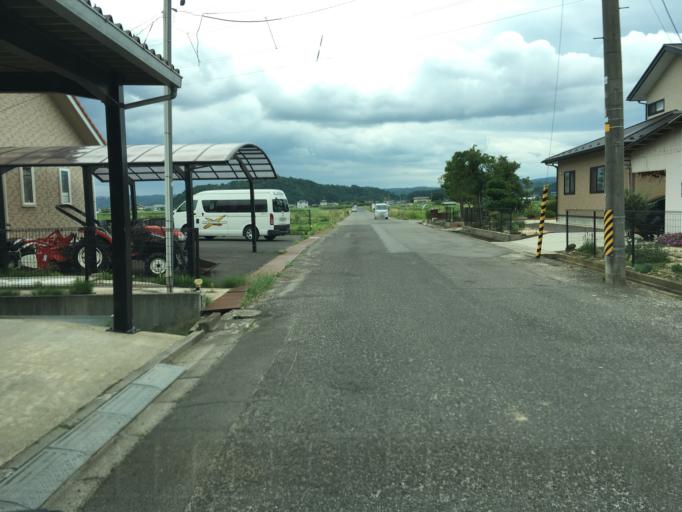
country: JP
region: Fukushima
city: Fukushima-shi
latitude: 37.7386
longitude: 140.4297
